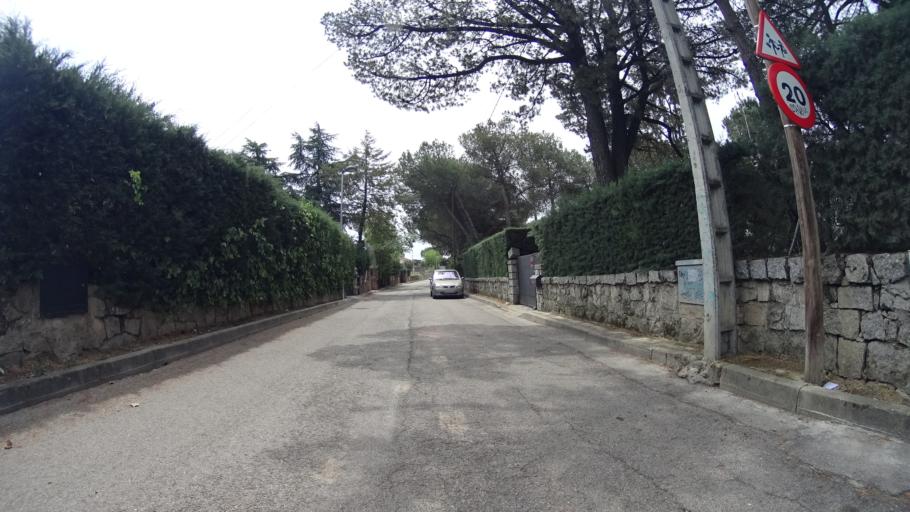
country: ES
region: Madrid
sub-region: Provincia de Madrid
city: Galapagar
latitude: 40.5710
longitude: -4.0015
